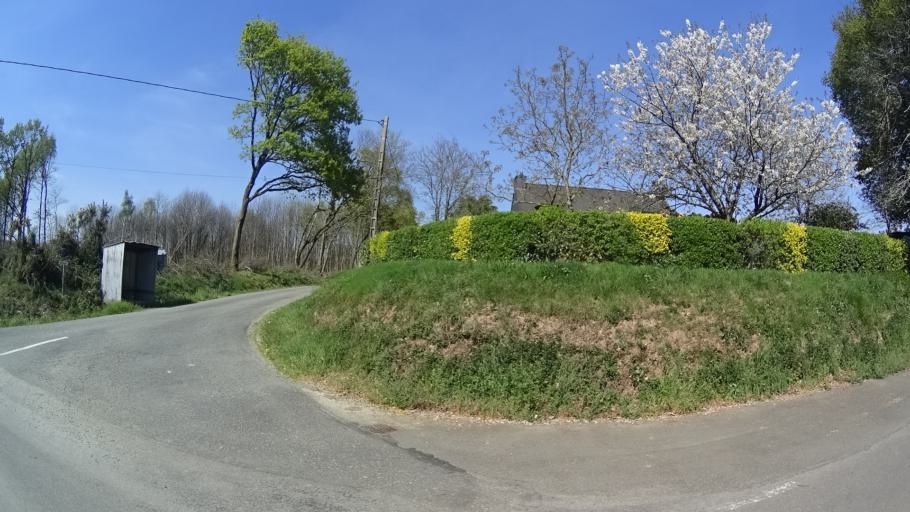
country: FR
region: Pays de la Loire
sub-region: Departement de la Loire-Atlantique
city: Fegreac
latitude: 47.5920
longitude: -2.0467
